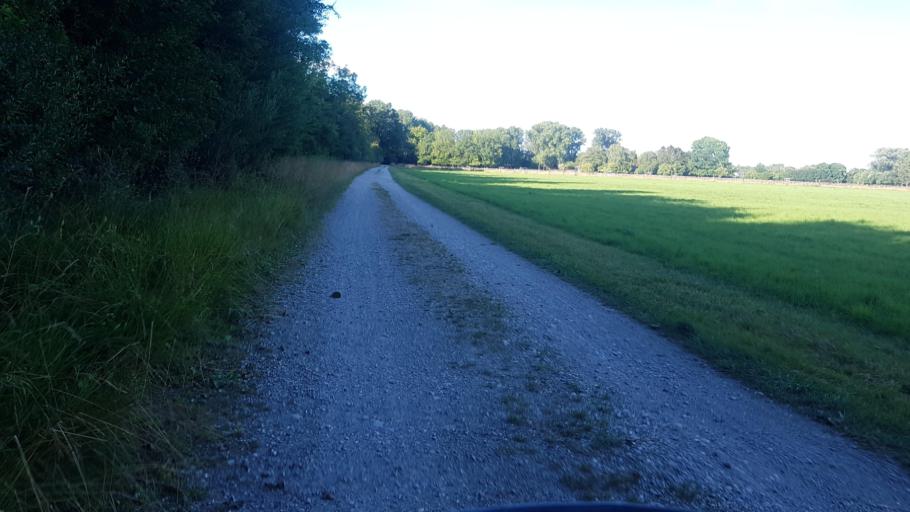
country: DE
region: Bavaria
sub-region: Upper Bavaria
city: Karlsfeld
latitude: 48.2418
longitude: 11.4983
